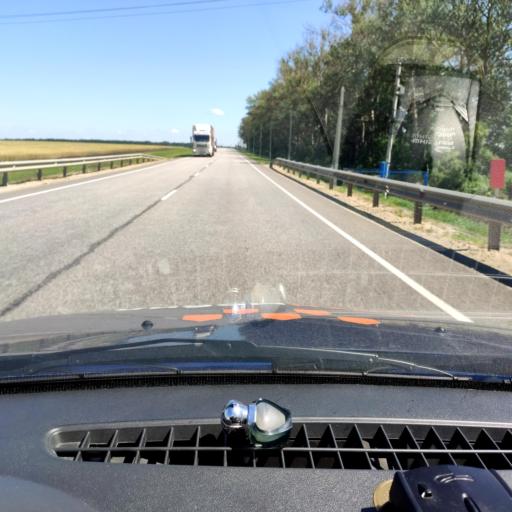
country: RU
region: Orjol
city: Pokrovskoye
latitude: 52.6308
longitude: 36.7019
